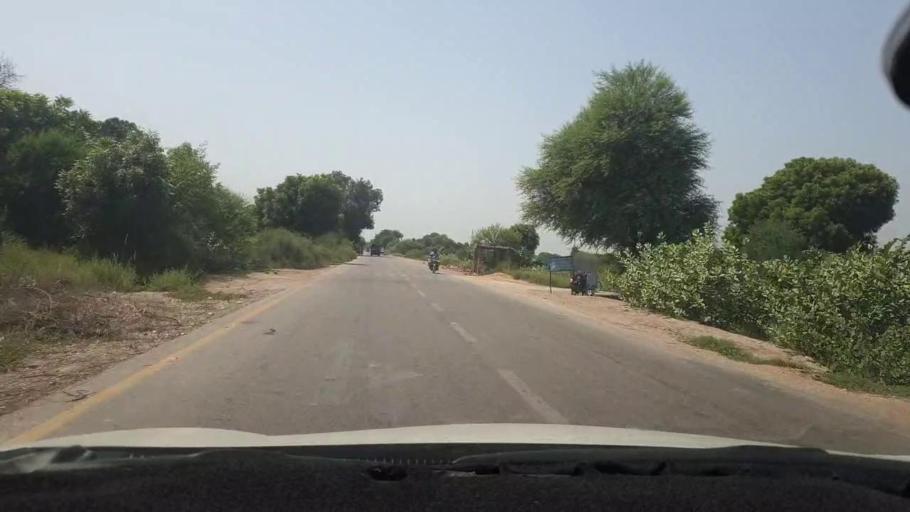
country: PK
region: Sindh
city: Bhit Shah
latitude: 25.8577
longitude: 68.5041
